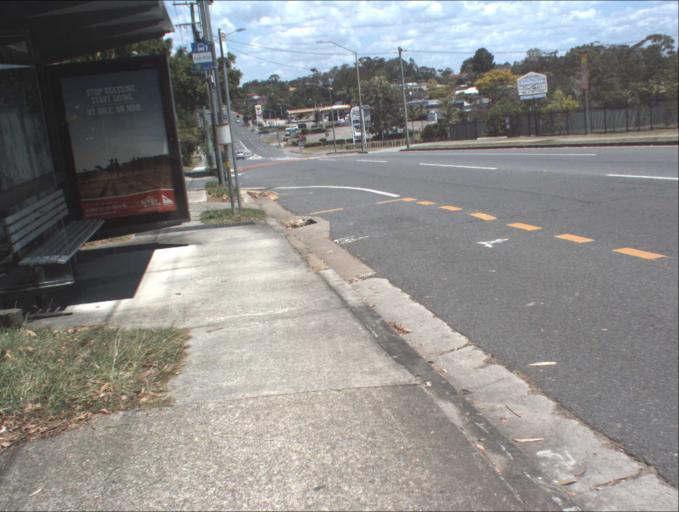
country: AU
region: Queensland
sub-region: Logan
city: Rochedale South
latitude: -27.5930
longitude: 153.1225
